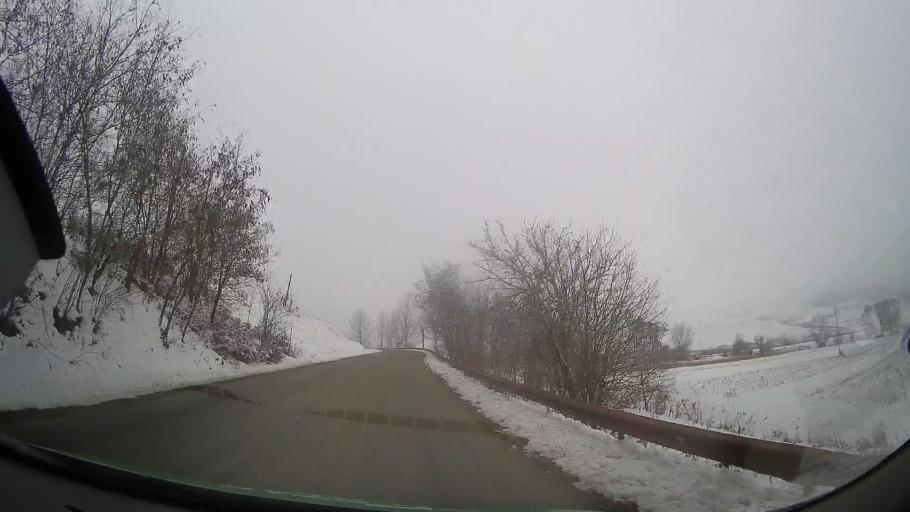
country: RO
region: Bacau
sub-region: Comuna Vultureni
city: Vultureni
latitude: 46.3969
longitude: 27.2776
